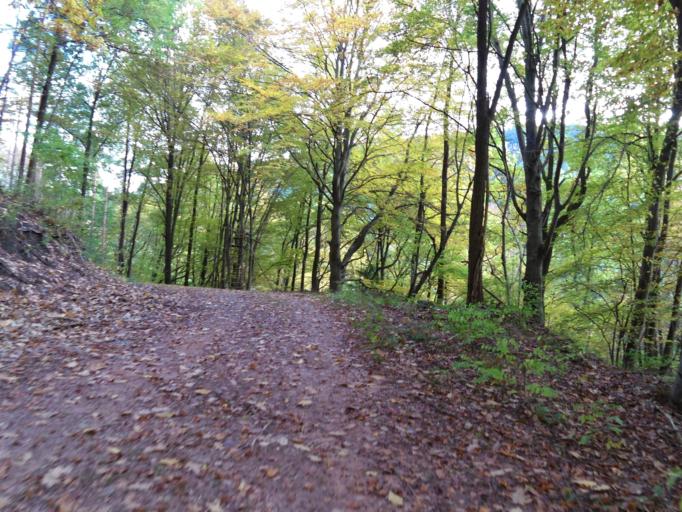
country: DE
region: Rheinland-Pfalz
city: Frankenstein
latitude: 49.4353
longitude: 7.9853
